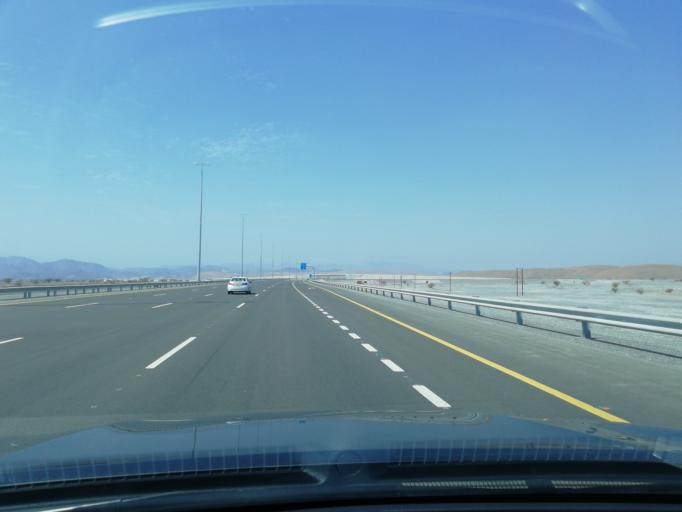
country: OM
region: Al Batinah
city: Bayt al `Awabi
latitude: 23.5335
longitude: 57.6707
